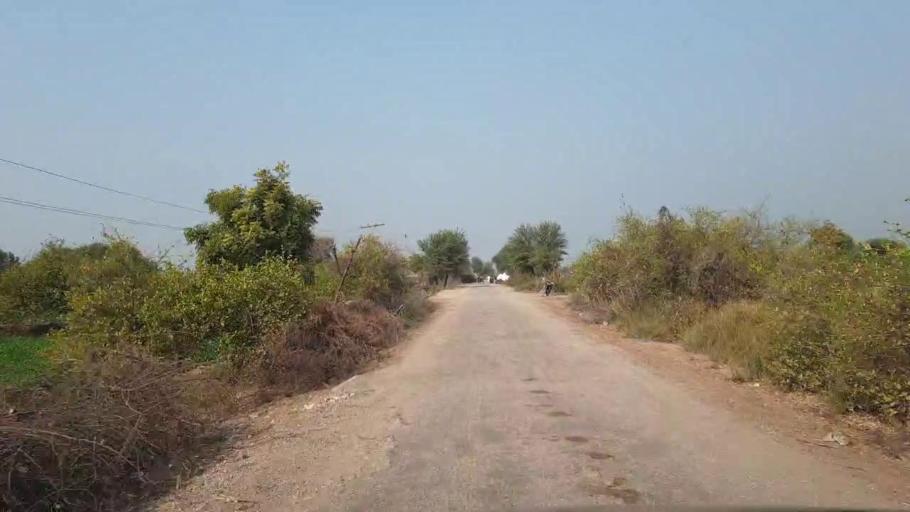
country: PK
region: Sindh
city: Hala
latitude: 25.8453
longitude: 68.4616
